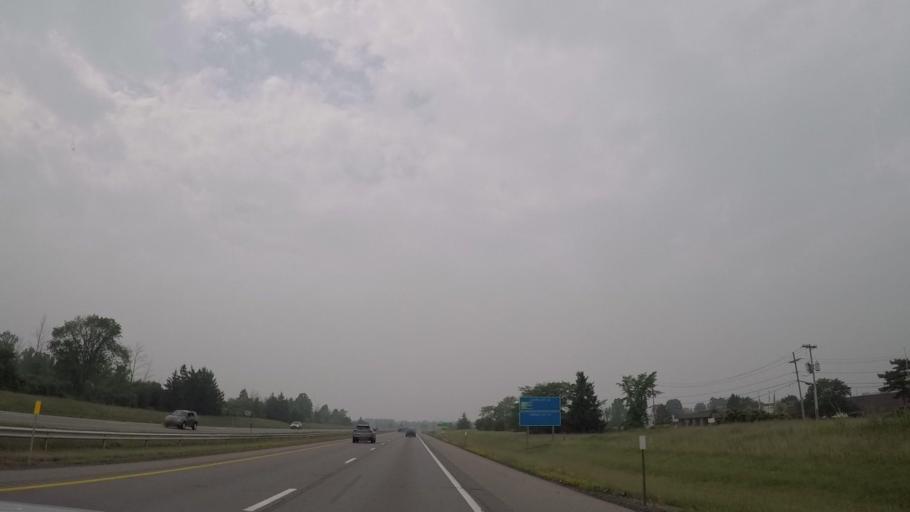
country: US
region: New York
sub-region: Erie County
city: Grandyle Village
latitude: 43.0388
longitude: -78.9858
